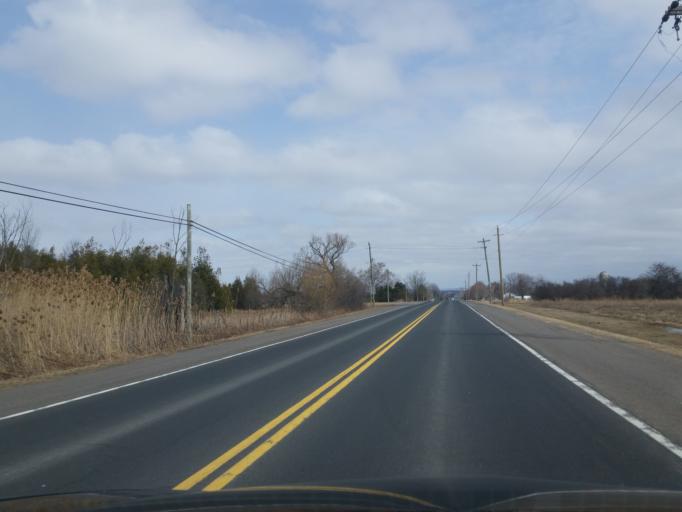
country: CA
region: Ontario
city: Cobourg
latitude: 43.9574
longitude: -78.4132
